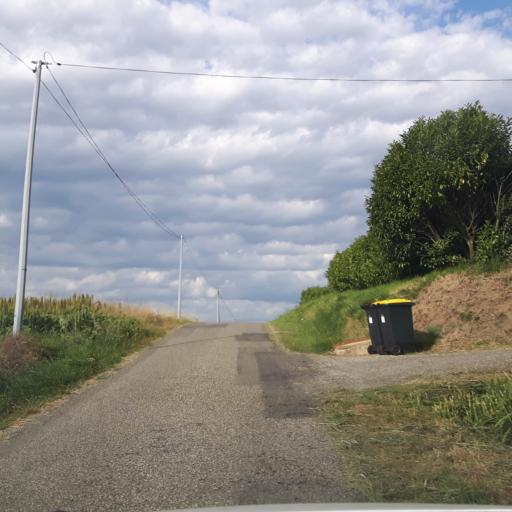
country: FR
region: Midi-Pyrenees
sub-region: Departement de la Haute-Garonne
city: Castelnau-d'Estretefonds
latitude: 43.7896
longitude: 1.3759
